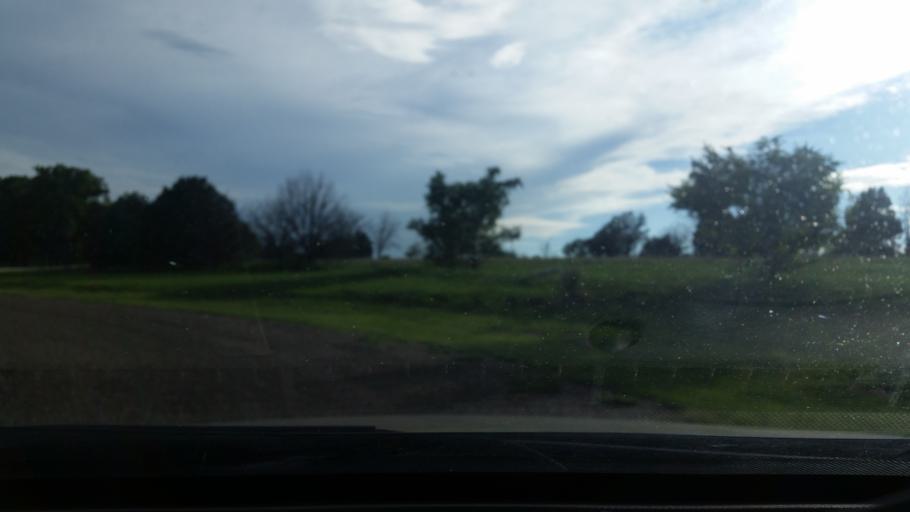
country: US
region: New Mexico
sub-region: Curry County
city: Clovis
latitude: 34.5225
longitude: -103.1936
